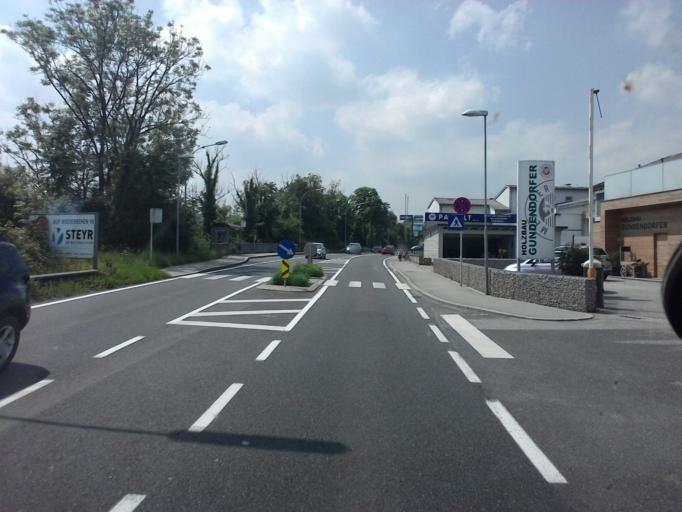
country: AT
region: Upper Austria
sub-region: Politischer Bezirk Steyr-Land
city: Garsten
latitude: 48.0432
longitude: 14.3845
